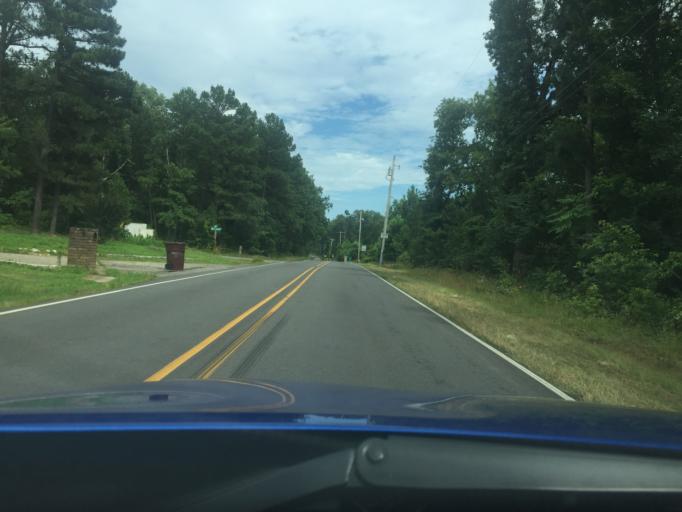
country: US
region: Arkansas
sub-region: Pulaski County
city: Maumelle
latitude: 34.8334
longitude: -92.4527
